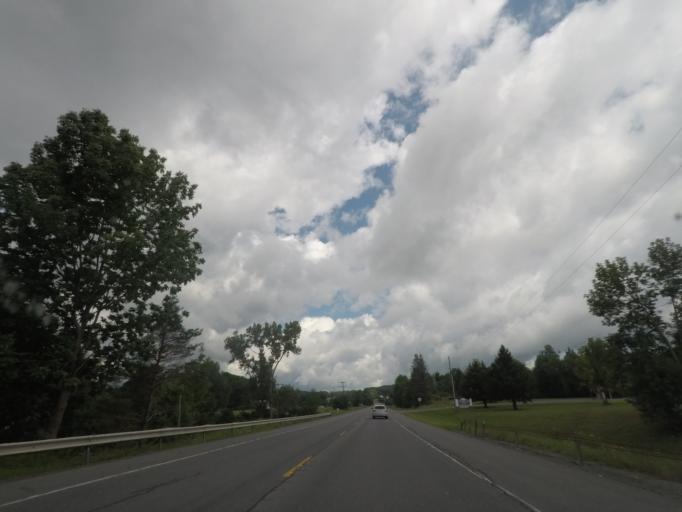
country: US
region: Massachusetts
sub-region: Berkshire County
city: Lanesborough
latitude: 42.5915
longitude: -73.3684
